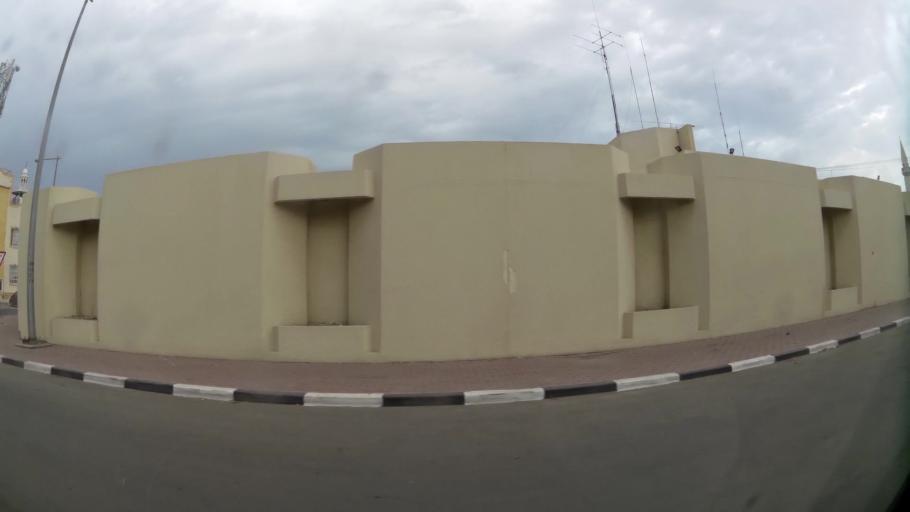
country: QA
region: Baladiyat ad Dawhah
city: Doha
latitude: 25.2711
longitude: 51.4976
